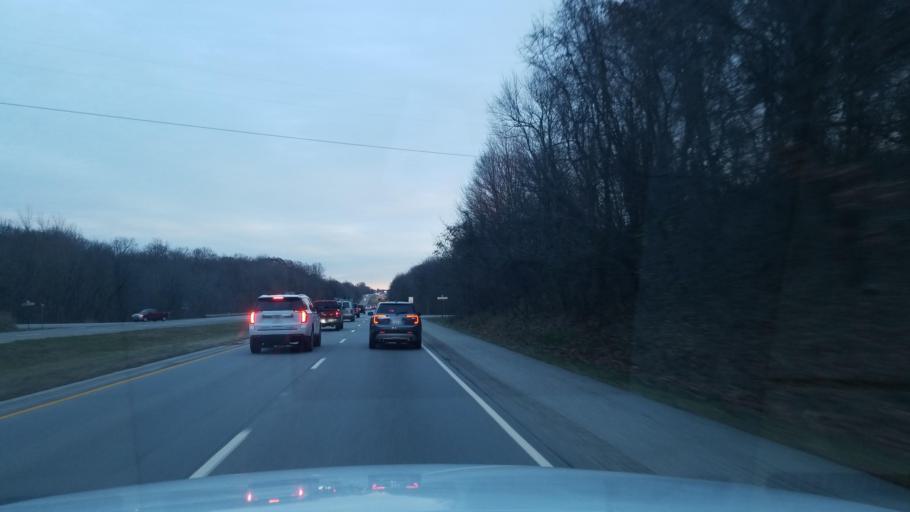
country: US
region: Indiana
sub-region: Vanderburgh County
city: Evansville
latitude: 37.9709
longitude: -87.6597
